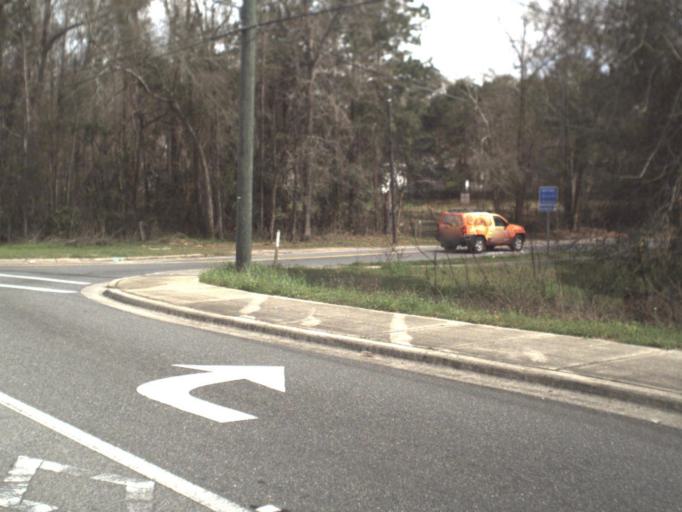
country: US
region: Florida
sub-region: Leon County
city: Tallahassee
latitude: 30.5380
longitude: -84.2302
